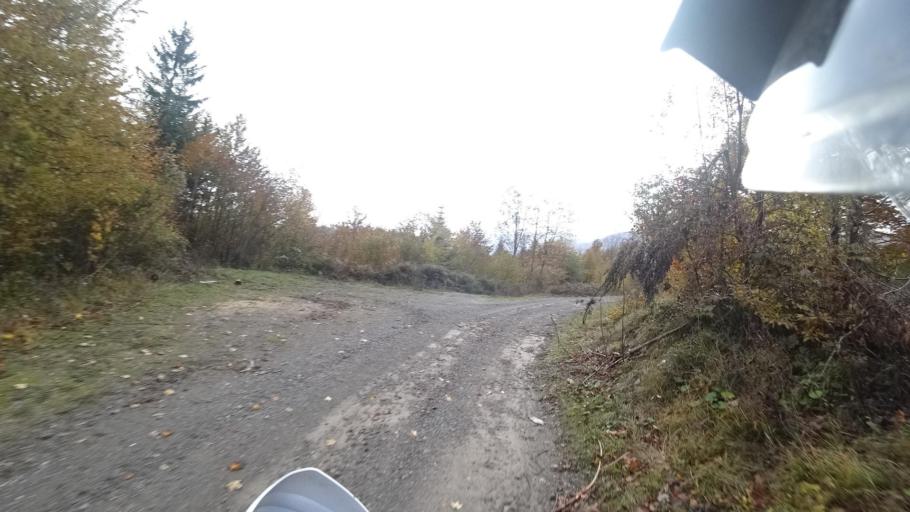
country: HR
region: Karlovacka
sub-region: Grad Ogulin
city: Ogulin
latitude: 45.1987
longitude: 15.1095
